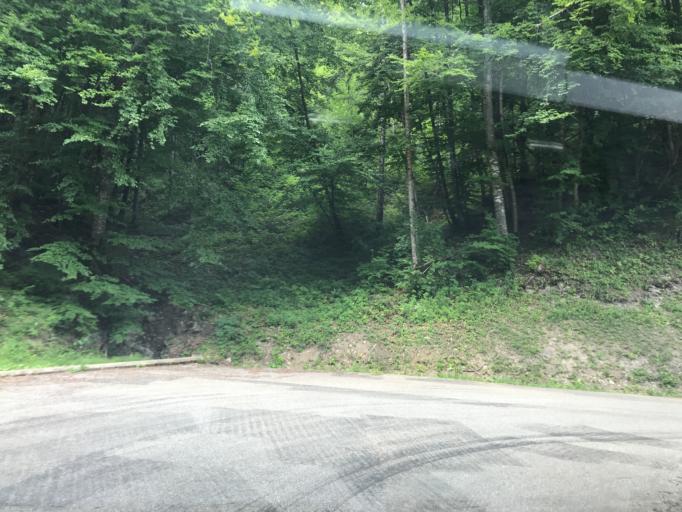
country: FR
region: Rhone-Alpes
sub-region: Departement de l'Isere
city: Barraux
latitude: 45.4369
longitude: 5.9607
